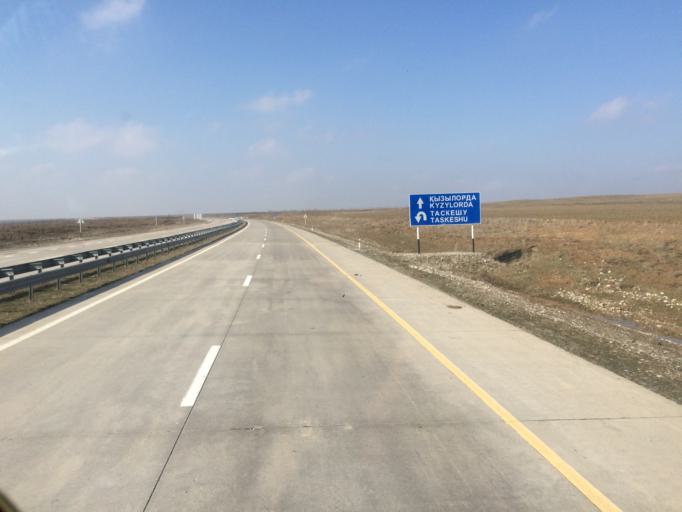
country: KZ
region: Ongtustik Qazaqstan
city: Shymkent
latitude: 42.4889
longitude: 69.5173
